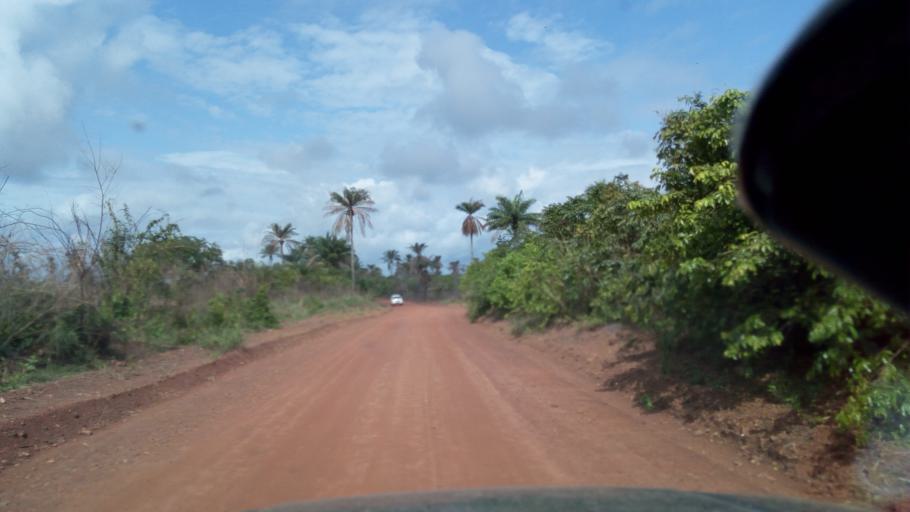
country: SL
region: Northern Province
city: Pepel
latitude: 8.6483
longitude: -13.0145
